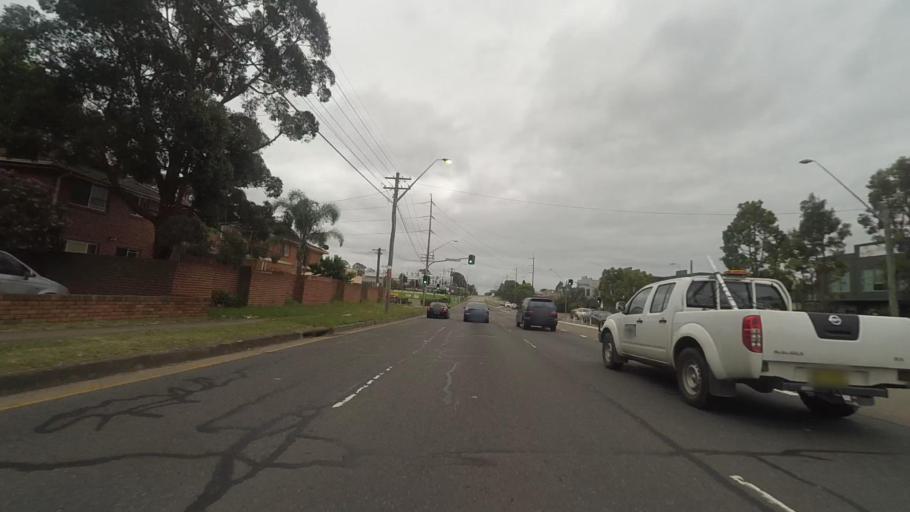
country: AU
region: New South Wales
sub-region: Bankstown
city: Bankstown
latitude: -33.8975
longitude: 151.0375
